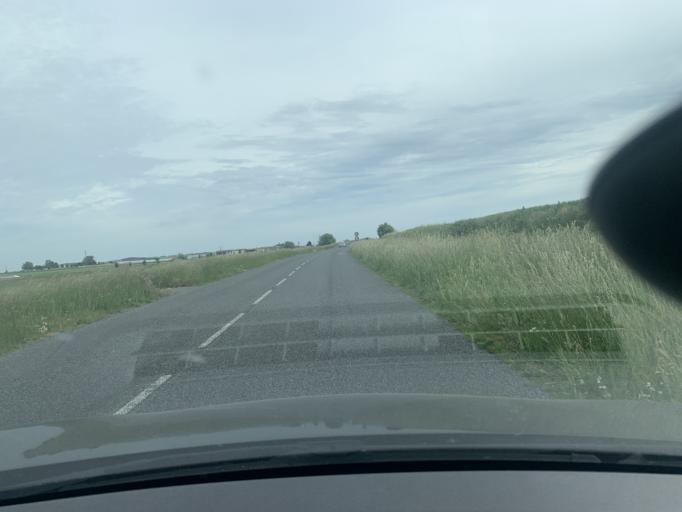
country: FR
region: Nord-Pas-de-Calais
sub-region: Departement du Nord
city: Rumilly-en-Cambresis
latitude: 50.1404
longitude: 3.2072
